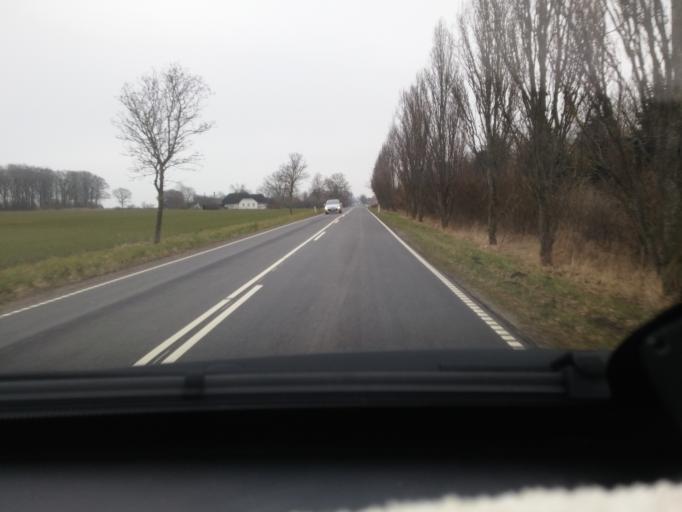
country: DK
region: South Denmark
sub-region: Kerteminde Kommune
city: Kerteminde
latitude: 55.4094
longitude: 10.7175
